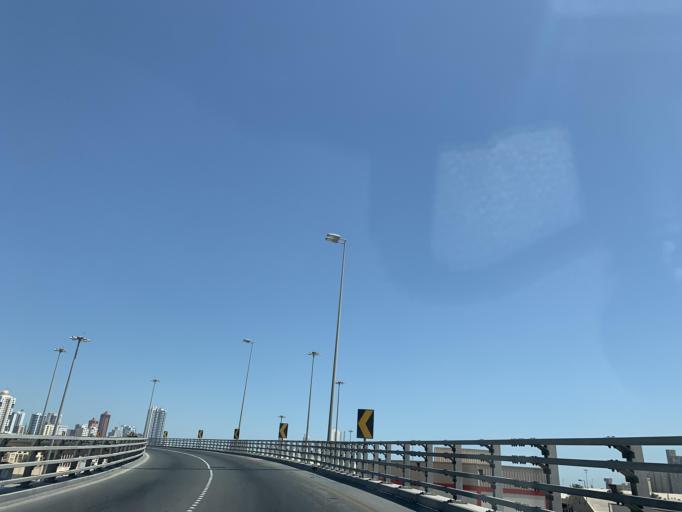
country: BH
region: Manama
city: Manama
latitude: 26.2007
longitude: 50.6001
